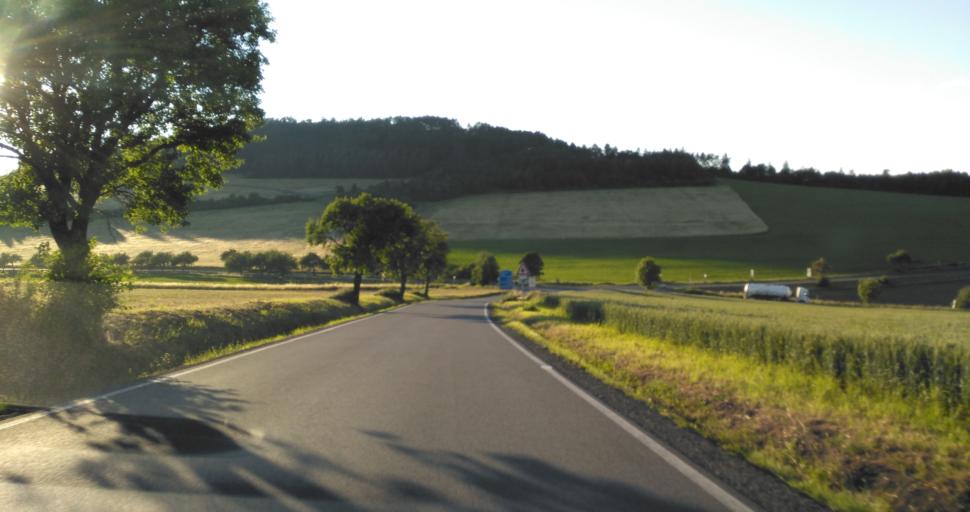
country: CZ
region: Central Bohemia
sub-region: Okres Beroun
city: Kraluv Dvur
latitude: 49.9144
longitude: 14.0318
